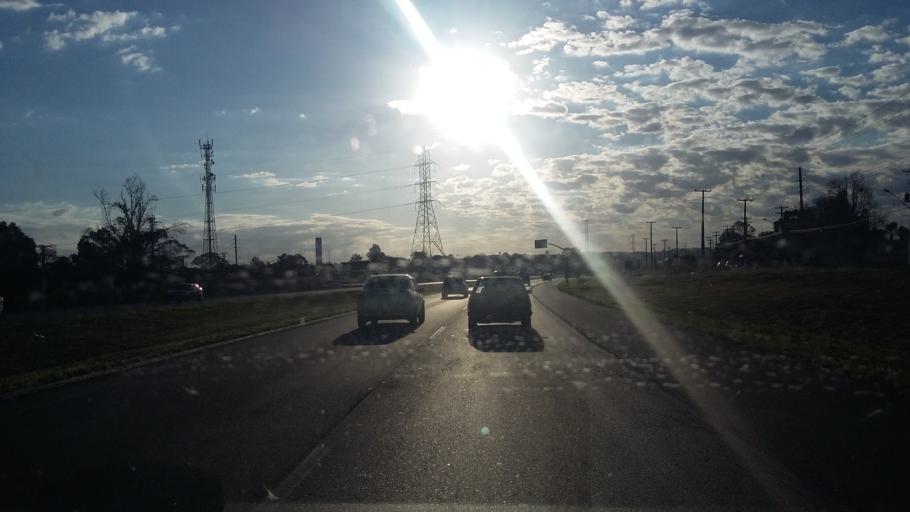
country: BR
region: Parana
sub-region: Araucaria
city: Araucaria
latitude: -25.5306
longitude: -49.3250
